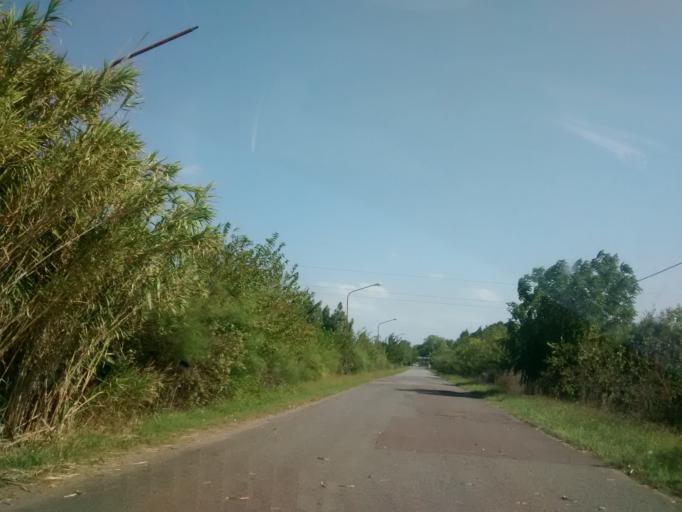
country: AR
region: Buenos Aires
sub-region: Partido de La Plata
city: La Plata
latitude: -35.0049
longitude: -57.9091
